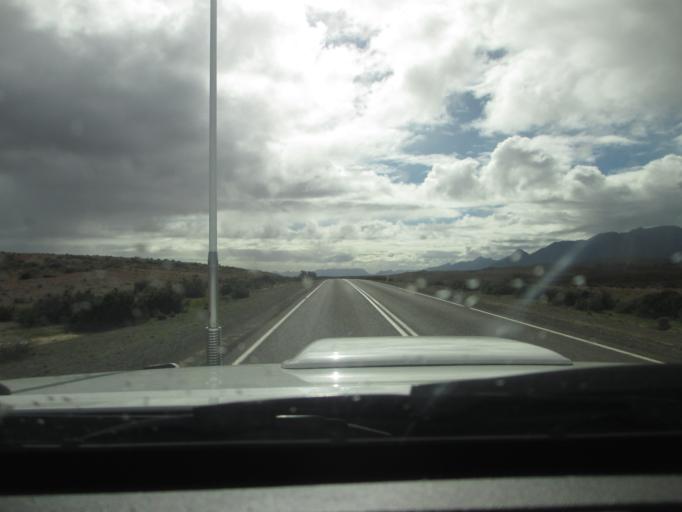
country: AU
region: South Australia
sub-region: Flinders Ranges
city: Quorn
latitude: -31.5855
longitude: 138.4162
